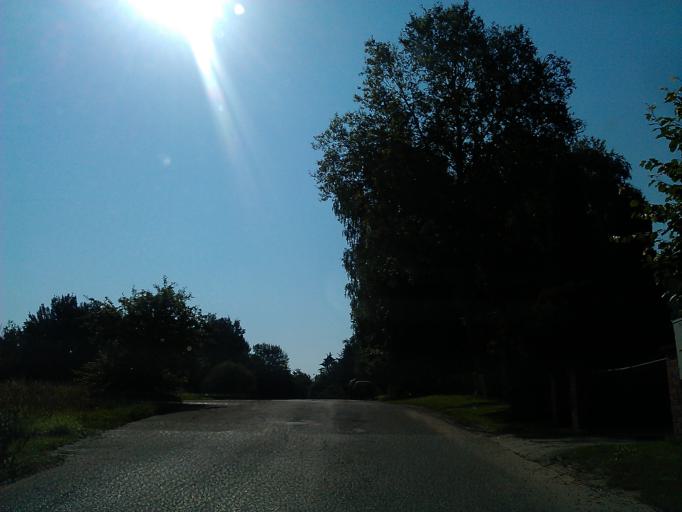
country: LV
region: Aizpute
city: Aizpute
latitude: 56.7174
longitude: 21.5944
